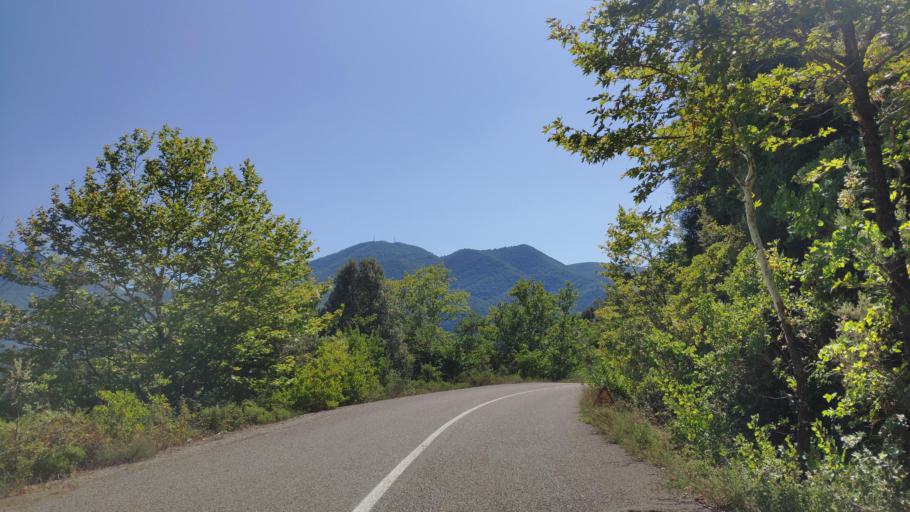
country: GR
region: Central Greece
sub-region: Nomos Evrytanias
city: Kerasochori
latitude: 39.0008
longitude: 21.5476
